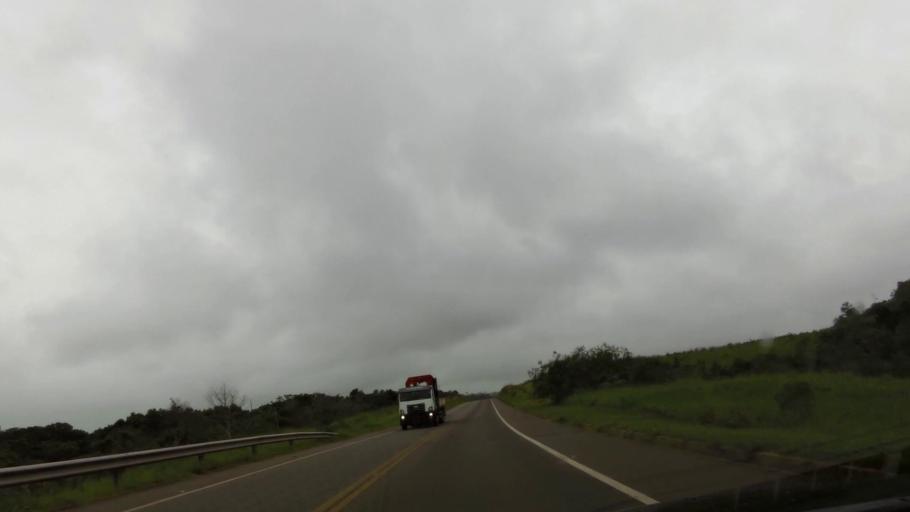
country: BR
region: Espirito Santo
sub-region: Guarapari
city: Guarapari
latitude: -20.7162
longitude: -40.5765
